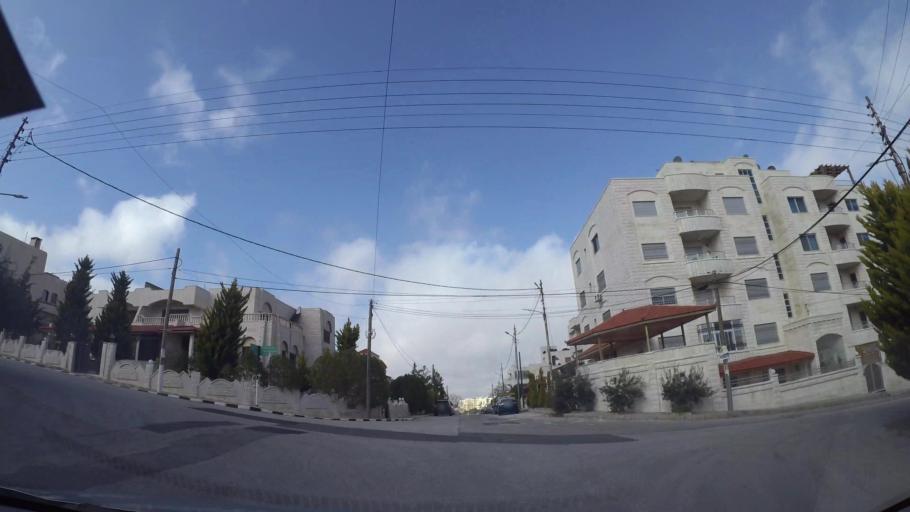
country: JO
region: Amman
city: Al Jubayhah
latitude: 32.0419
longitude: 35.8710
